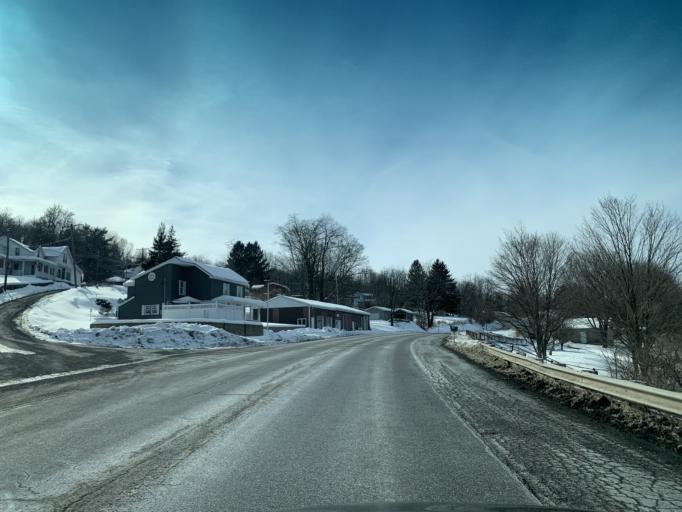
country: US
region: Maryland
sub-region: Allegany County
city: Frostburg
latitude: 39.6196
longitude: -78.9051
